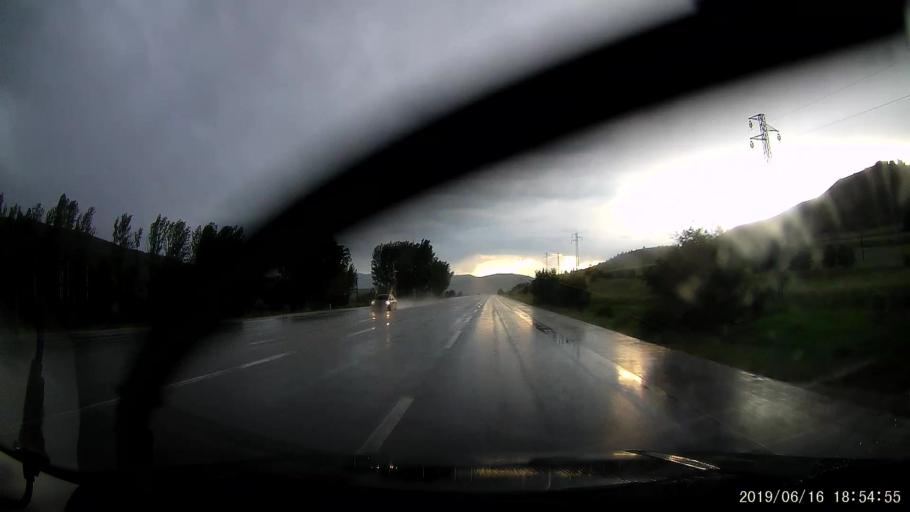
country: TR
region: Erzincan
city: Refahiye
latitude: 39.8984
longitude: 38.8417
